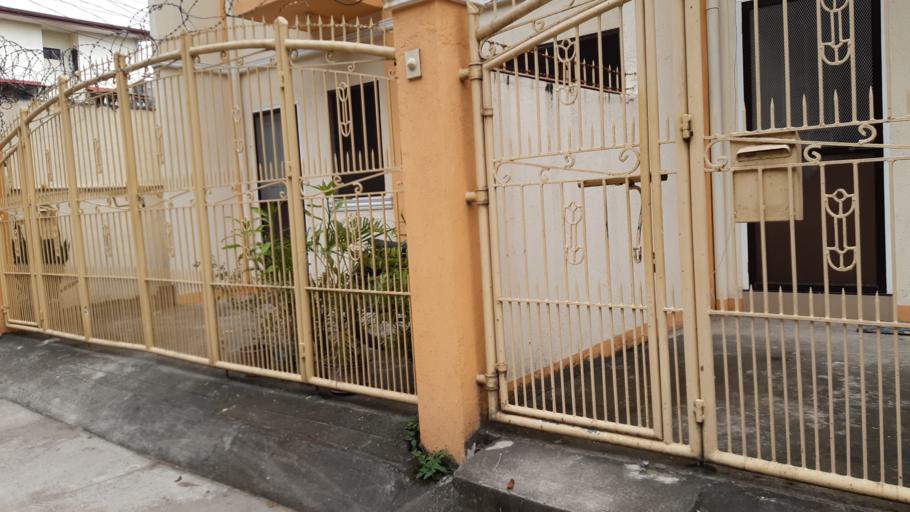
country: PH
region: Central Visayas
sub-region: Province of Negros Oriental
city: Dumaguete
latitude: 9.3048
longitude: 123.2984
